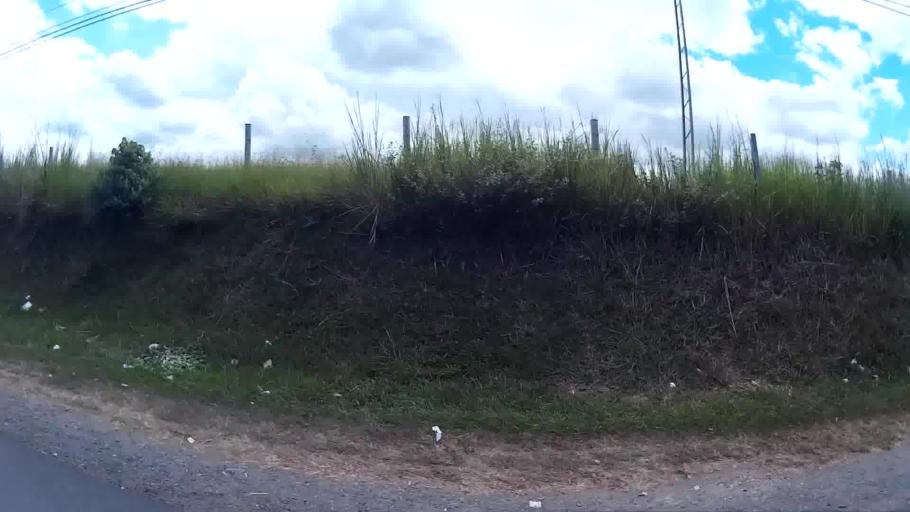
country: CO
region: Risaralda
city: Pereira
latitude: 4.8124
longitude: -75.7735
